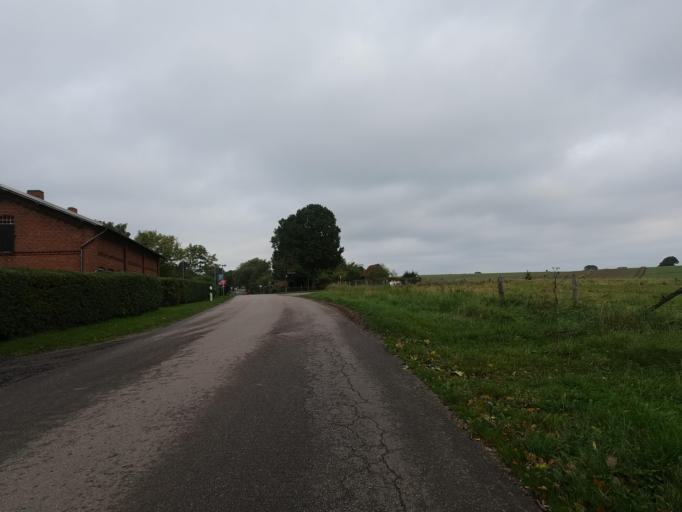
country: DE
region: Schleswig-Holstein
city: Neukirchen
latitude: 54.3335
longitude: 11.0303
